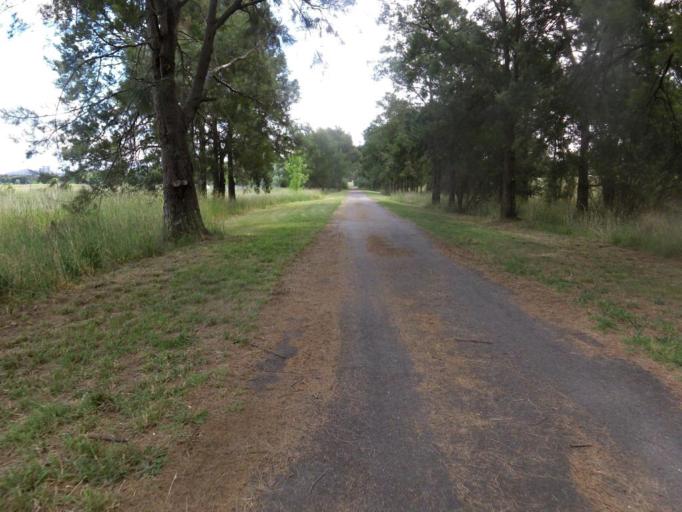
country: AU
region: Australian Capital Territory
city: Belconnen
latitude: -35.2172
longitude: 149.0838
